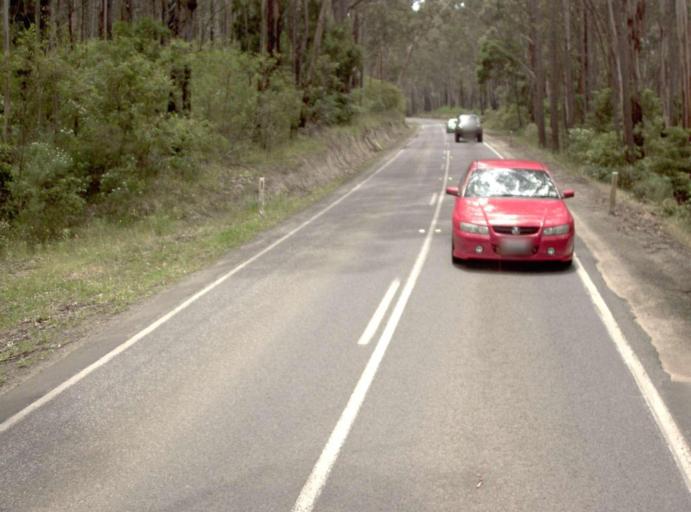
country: AU
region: Victoria
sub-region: Latrobe
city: Traralgon
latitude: -38.4289
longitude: 146.7423
